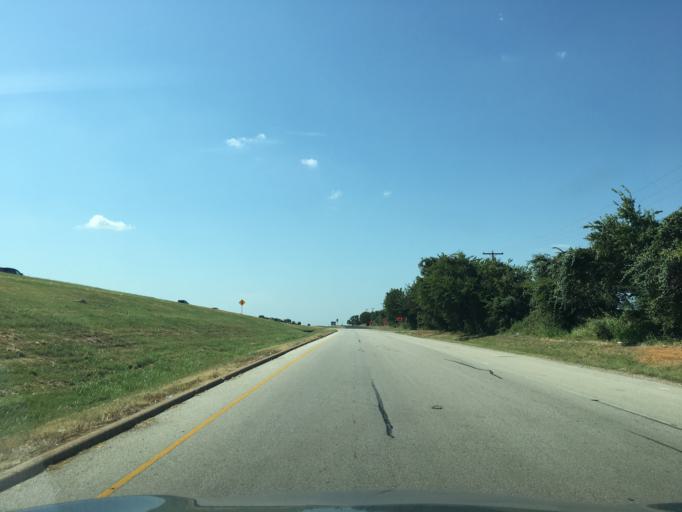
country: US
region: Texas
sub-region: Tarrant County
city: Kennedale
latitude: 32.6342
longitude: -97.1764
